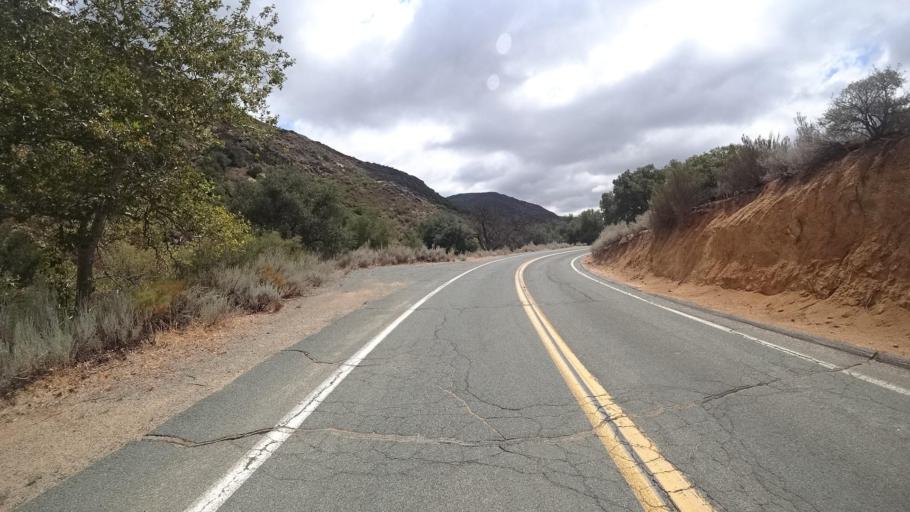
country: US
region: California
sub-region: San Diego County
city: Pine Valley
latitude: 32.7722
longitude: -116.4505
